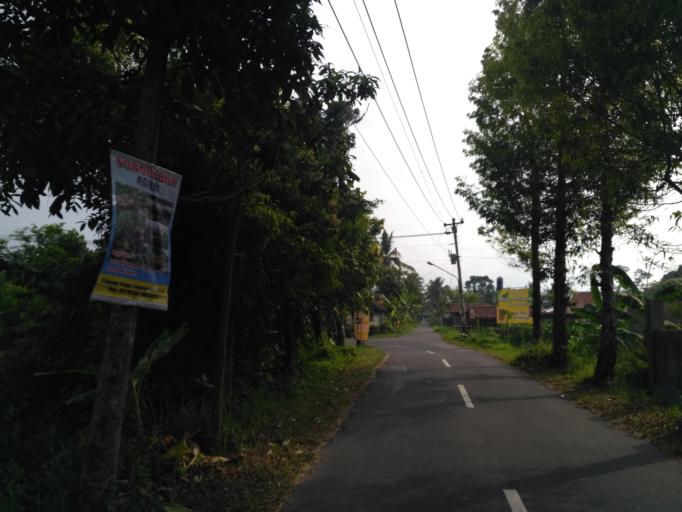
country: ID
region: Daerah Istimewa Yogyakarta
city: Melati
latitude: -7.7114
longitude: 110.3975
